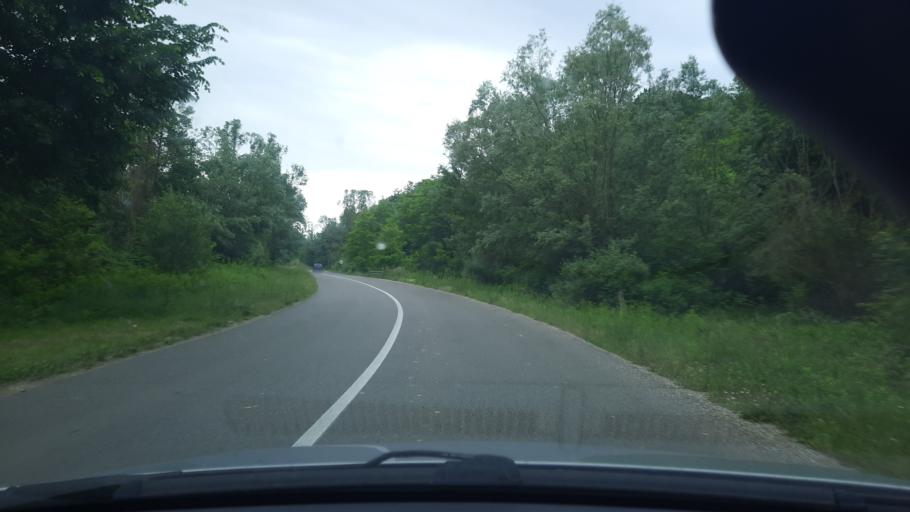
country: RS
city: Jarebice
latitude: 44.4984
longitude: 19.4852
